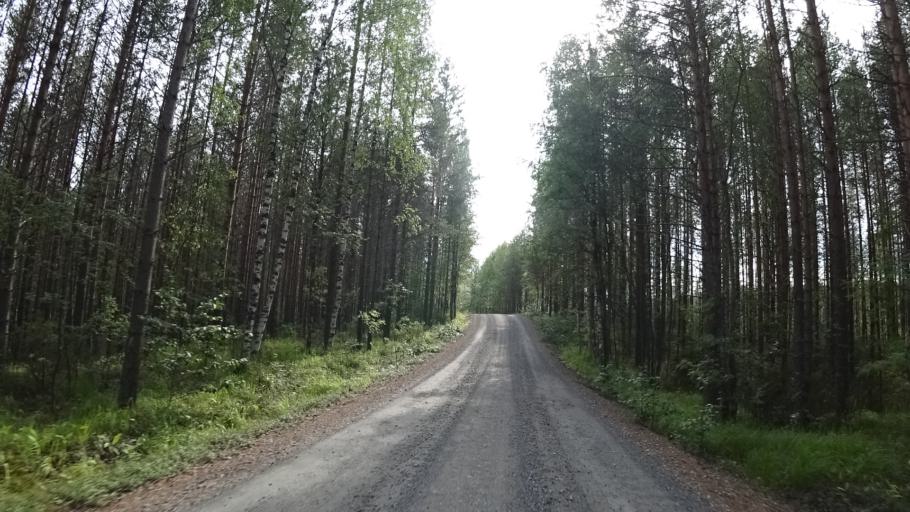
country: FI
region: North Karelia
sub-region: Joensuu
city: Ilomantsi
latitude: 62.6119
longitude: 31.1885
